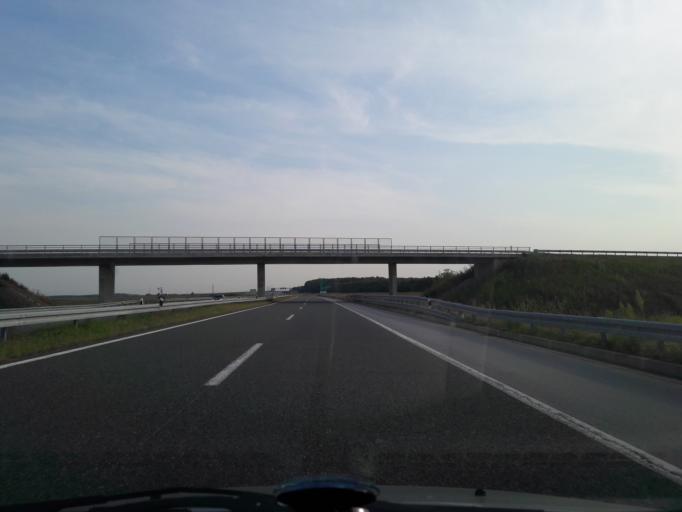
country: HR
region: Osjecko-Baranjska
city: Cepin
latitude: 45.5167
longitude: 18.5084
